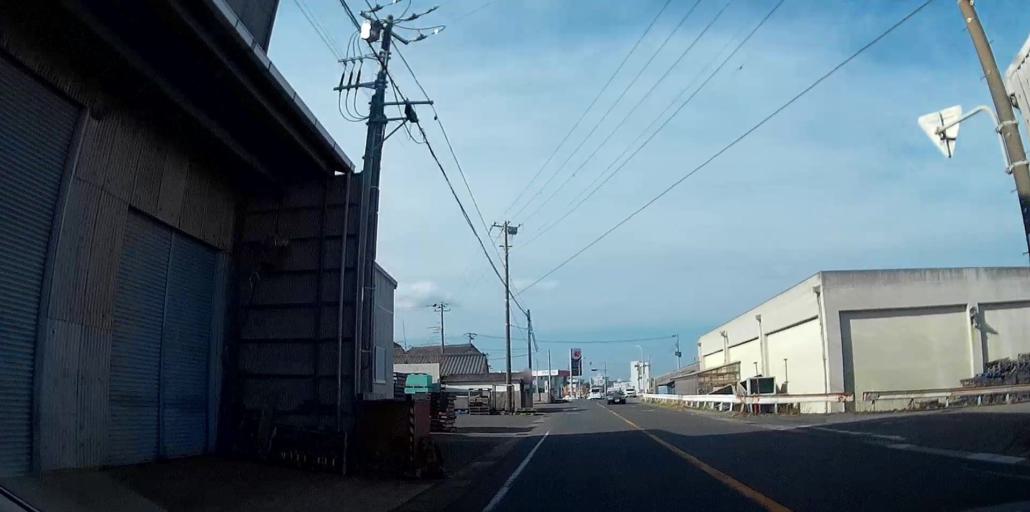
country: JP
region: Chiba
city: Tateyama
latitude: 34.9530
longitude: 139.9636
